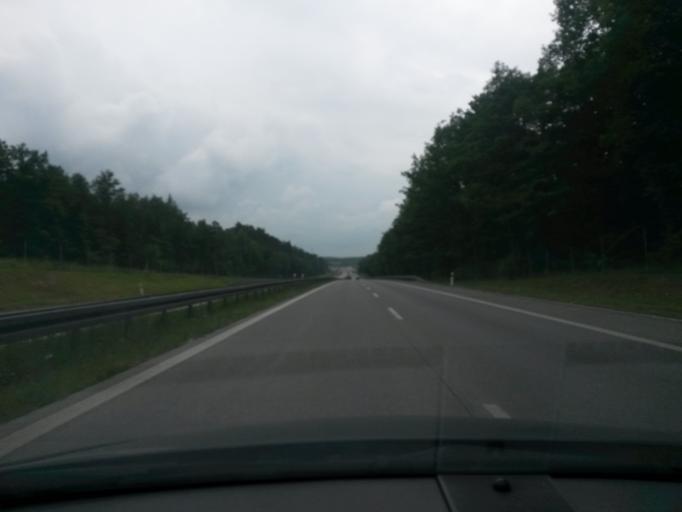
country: PL
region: Lodz Voivodeship
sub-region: Powiat rawski
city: Regnow
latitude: 51.8336
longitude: 20.3376
